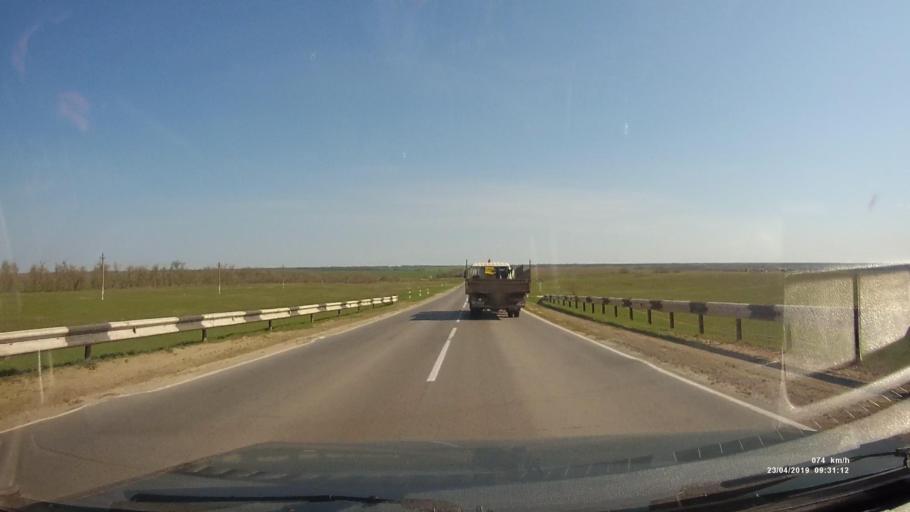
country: RU
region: Rostov
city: Gundorovskiy
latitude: 46.7784
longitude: 41.8226
